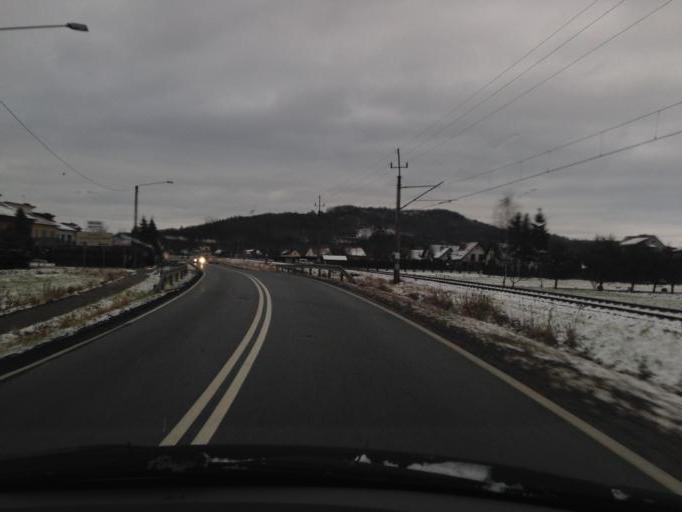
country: PL
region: Lesser Poland Voivodeship
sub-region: Powiat tarnowski
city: Gromnik
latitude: 49.8404
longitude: 20.9715
